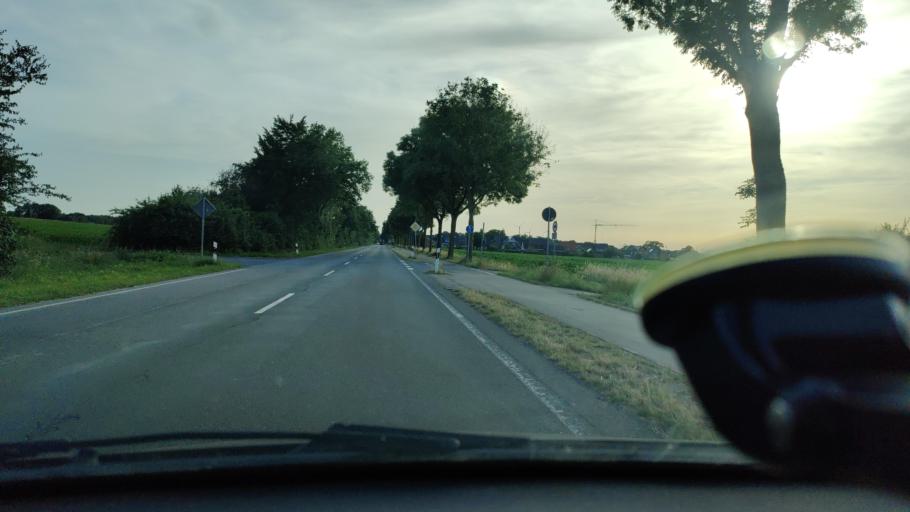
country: DE
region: North Rhine-Westphalia
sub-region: Regierungsbezirk Munster
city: Legden
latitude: 52.0090
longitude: 7.1485
